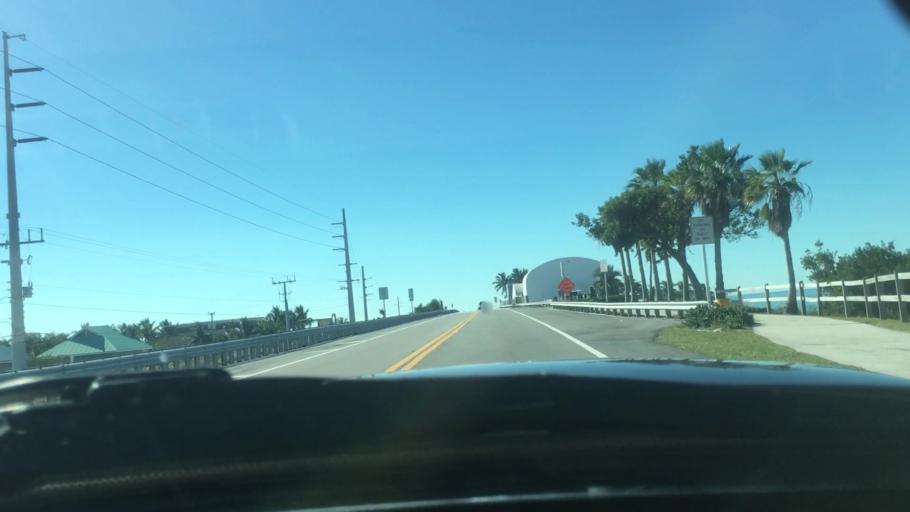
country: US
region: Florida
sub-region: Monroe County
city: Marathon
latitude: 24.7073
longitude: -81.1221
